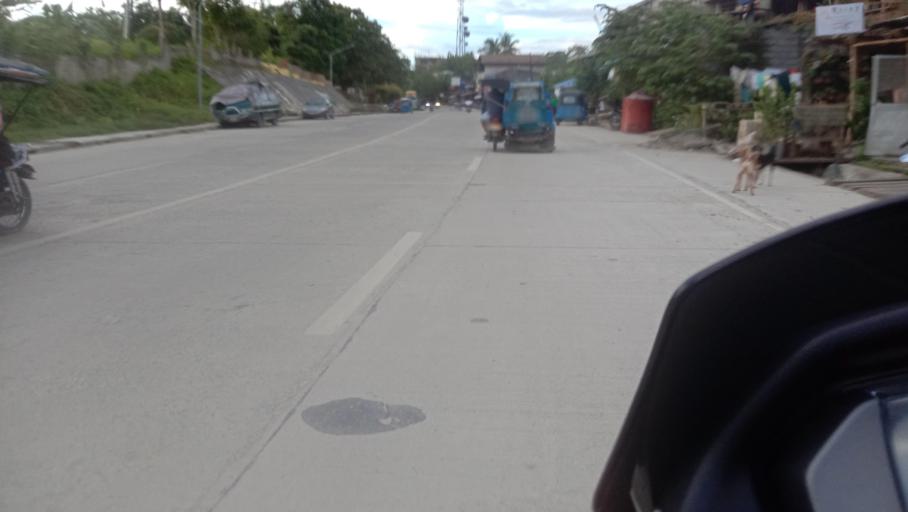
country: PH
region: Caraga
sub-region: Province of Surigao del Sur
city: Barobo
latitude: 8.5262
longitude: 126.1199
